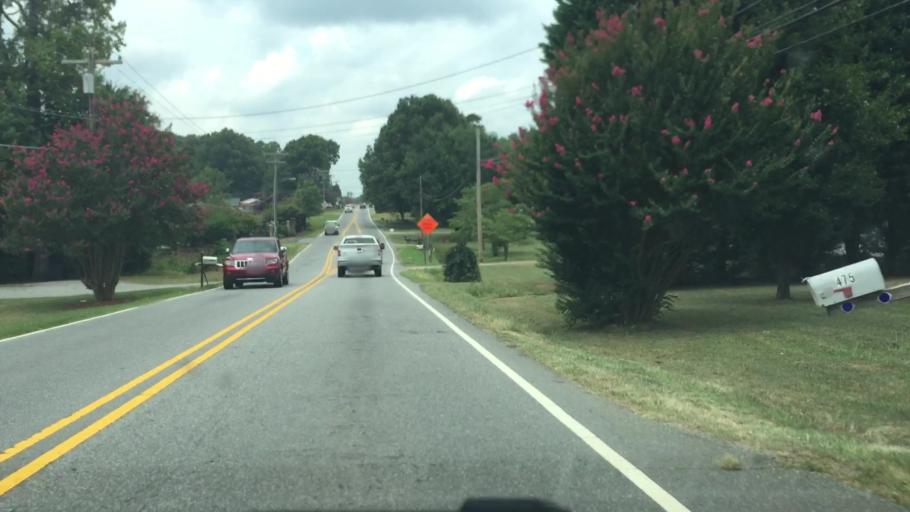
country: US
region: North Carolina
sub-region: Iredell County
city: Troutman
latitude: 35.6962
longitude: -80.8768
